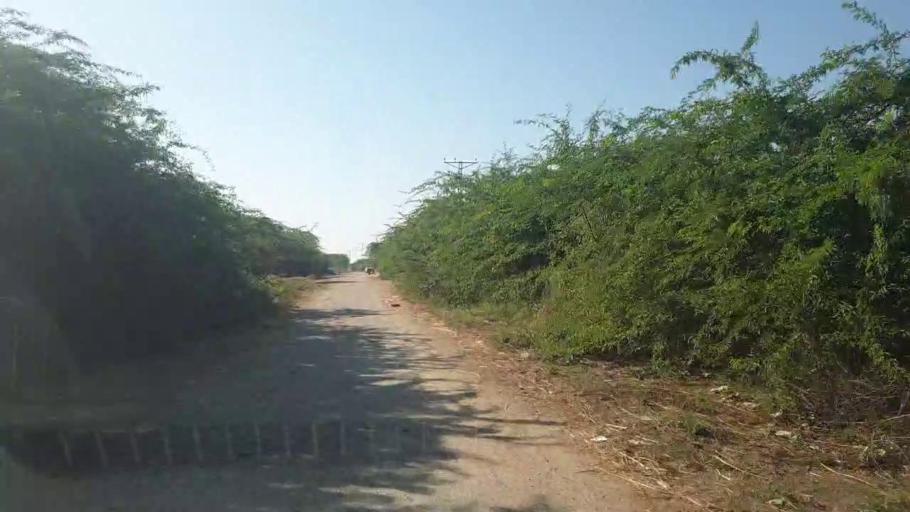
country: PK
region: Sindh
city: Talhar
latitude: 24.9482
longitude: 68.7937
